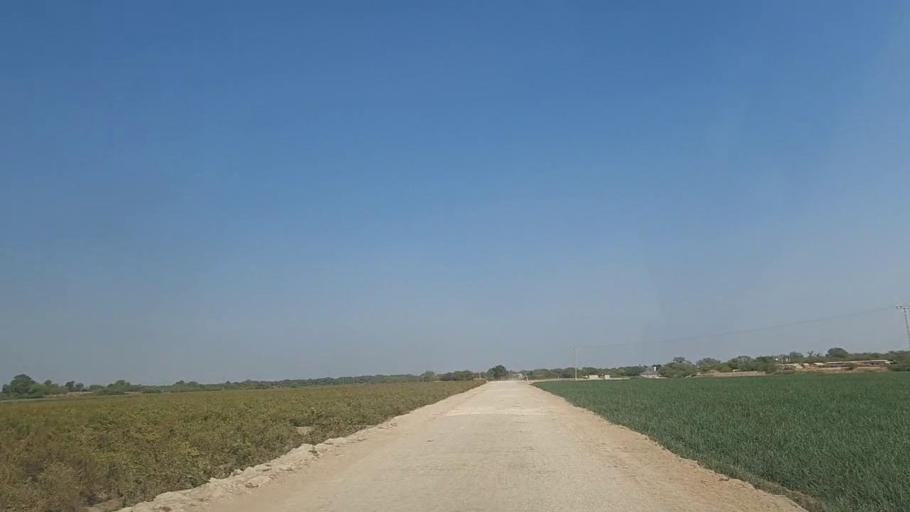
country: PK
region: Sindh
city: Digri
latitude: 25.1676
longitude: 69.1962
